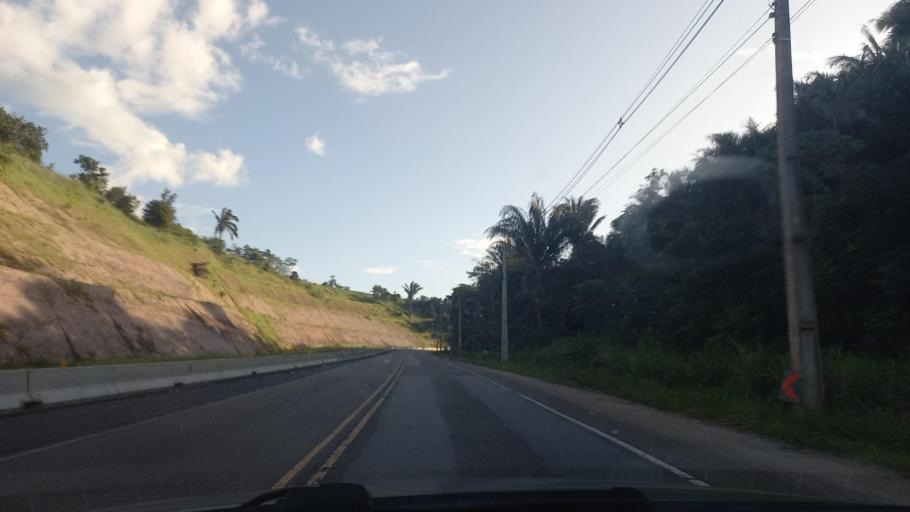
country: BR
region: Alagoas
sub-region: Campo Alegre
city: Campo Alegre
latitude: -9.8215
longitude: -36.2234
